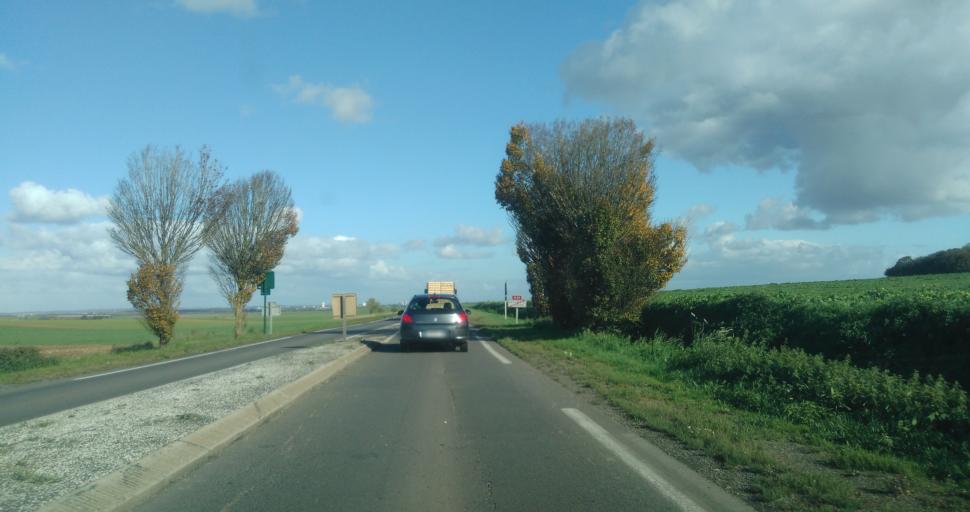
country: FR
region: Nord-Pas-de-Calais
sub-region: Departement du Pas-de-Calais
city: Beaumetz-les-Loges
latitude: 50.2461
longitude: 2.6680
